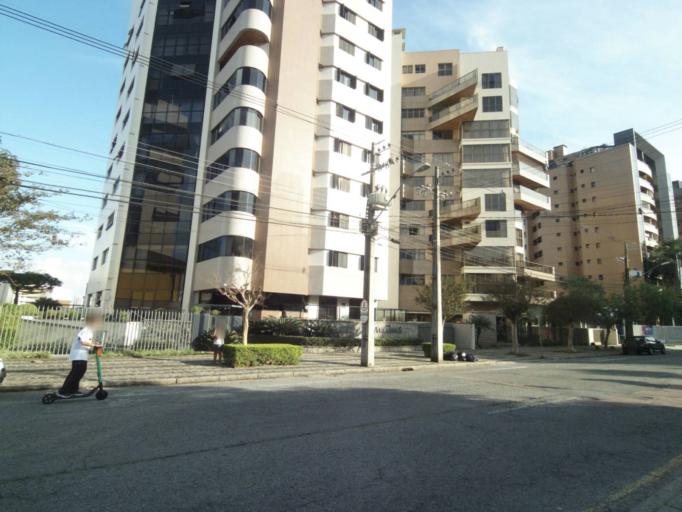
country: BR
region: Parana
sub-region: Curitiba
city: Curitiba
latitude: -25.4320
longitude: -49.2905
